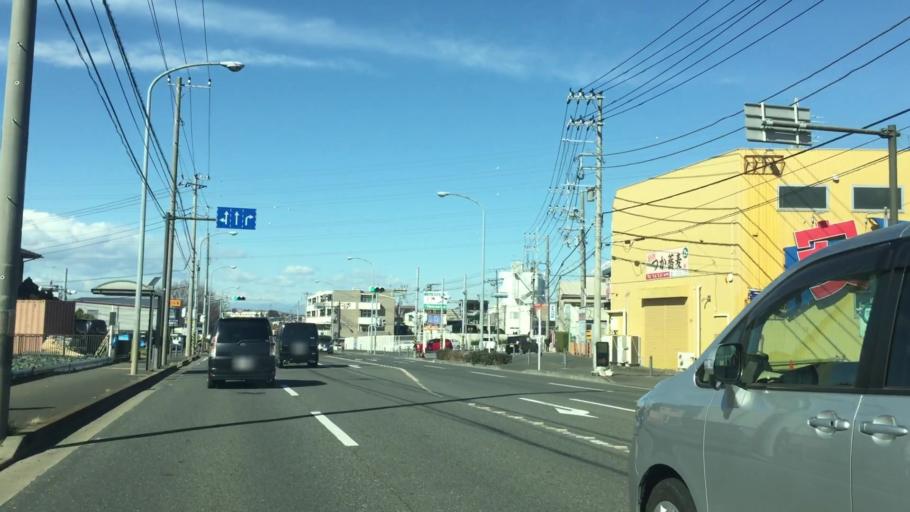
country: JP
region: Kanagawa
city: Yokohama
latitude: 35.4825
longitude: 139.5984
